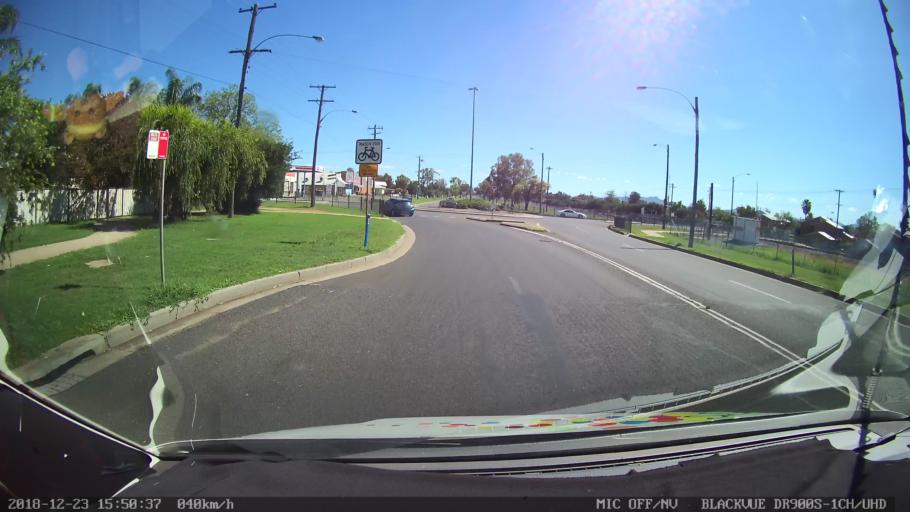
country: AU
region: New South Wales
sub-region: Tamworth Municipality
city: South Tamworth
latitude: -31.1074
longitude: 150.8998
